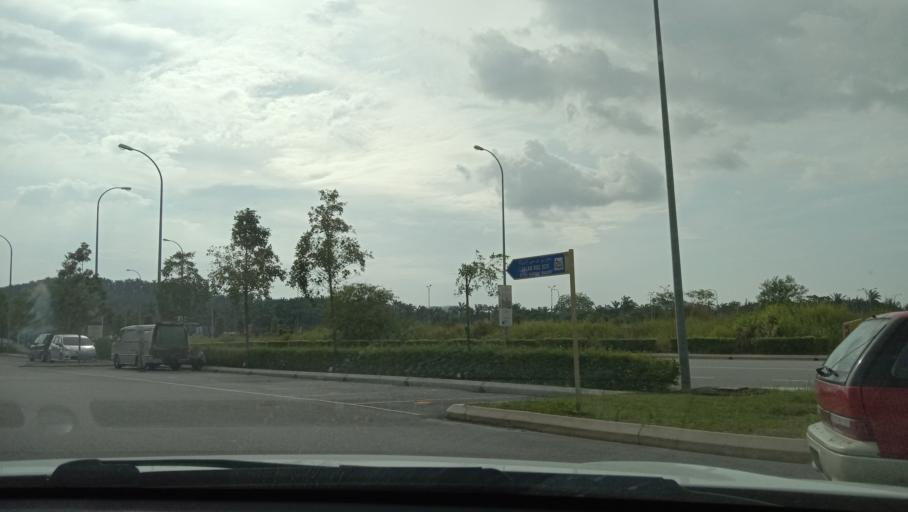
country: MY
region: Selangor
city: Ladang Seri Kundang
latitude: 3.2437
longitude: 101.4752
